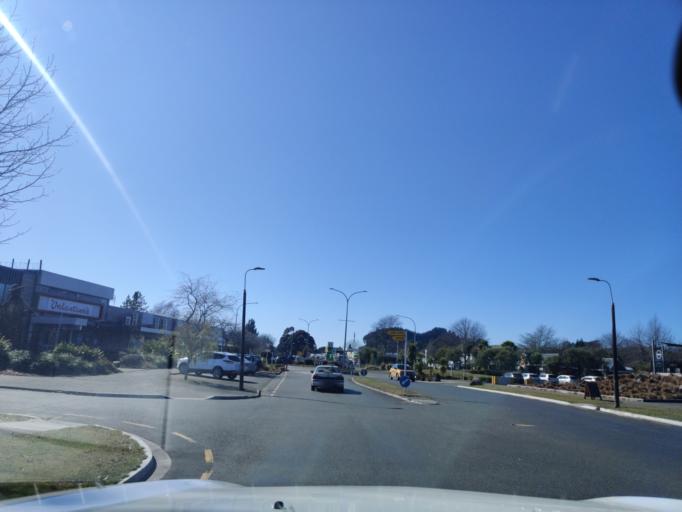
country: NZ
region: Waikato
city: Turangi
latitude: -38.9897
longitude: 175.8087
